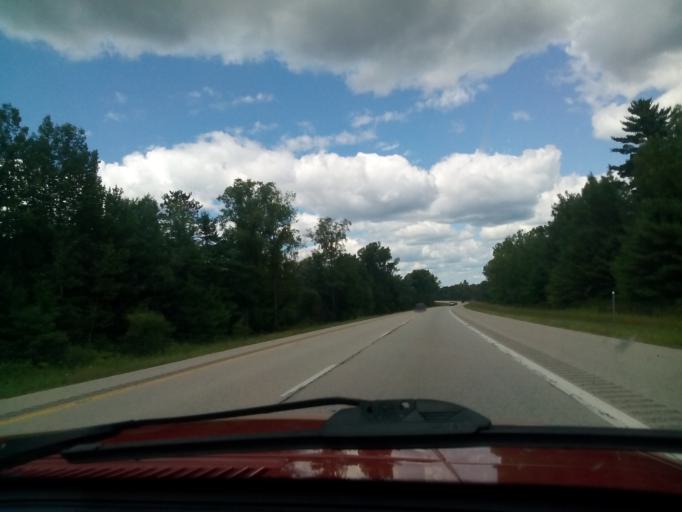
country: US
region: Michigan
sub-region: Ogemaw County
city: Skidway Lake
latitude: 44.0678
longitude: -84.0886
